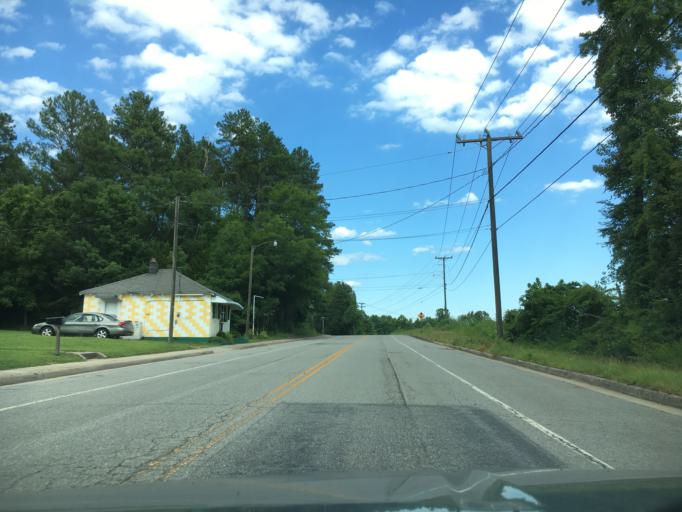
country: US
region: Virginia
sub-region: Halifax County
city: South Boston
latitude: 36.7112
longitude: -78.8878
